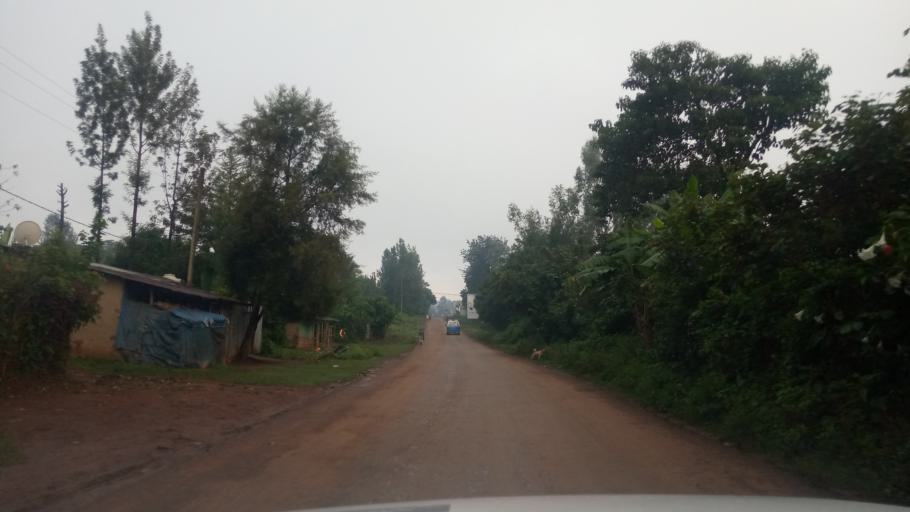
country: ET
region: Oromiya
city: Jima
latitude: 7.6924
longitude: 36.8234
